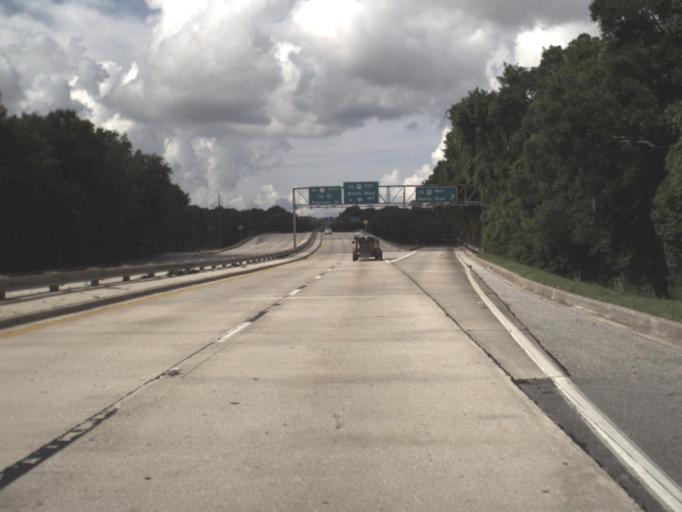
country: US
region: Florida
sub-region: Duval County
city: Jacksonville
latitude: 30.2992
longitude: -81.6133
